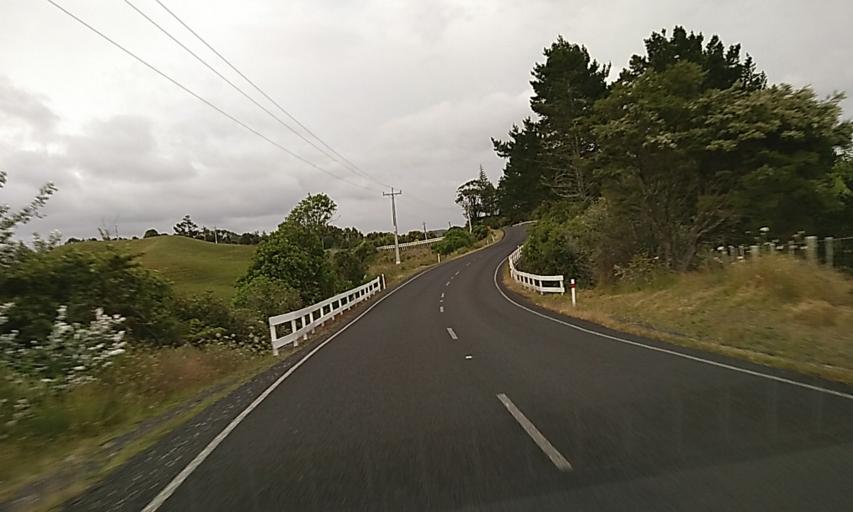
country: NZ
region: Auckland
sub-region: Auckland
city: Pukekohe East
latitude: -37.3191
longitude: 174.9339
